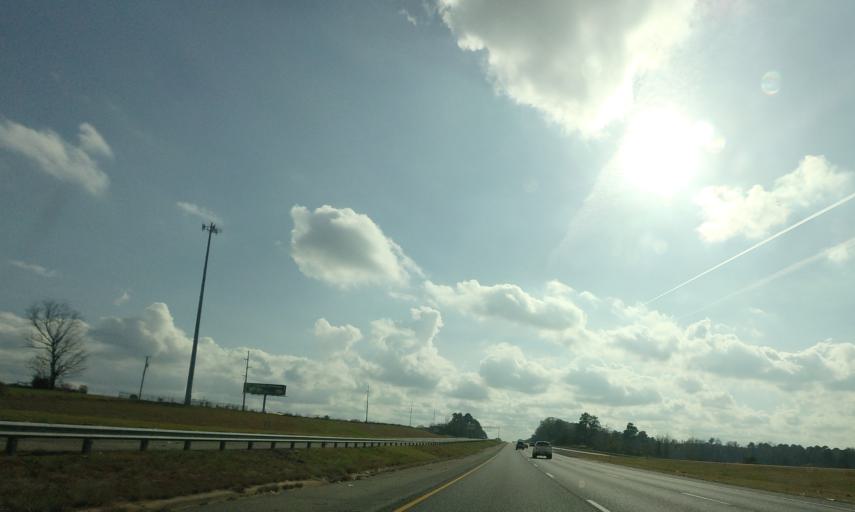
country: US
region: Georgia
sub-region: Houston County
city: Perry
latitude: 32.5435
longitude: -83.7441
